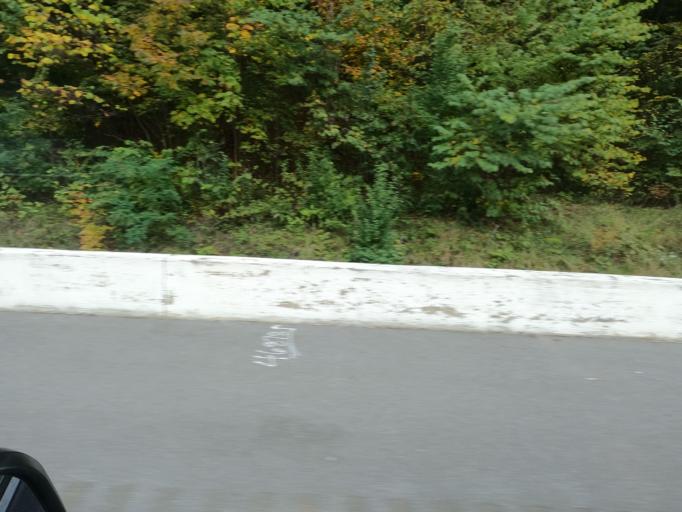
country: US
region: Tennessee
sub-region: Carter County
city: Elizabethton
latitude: 36.2744
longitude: -82.2307
